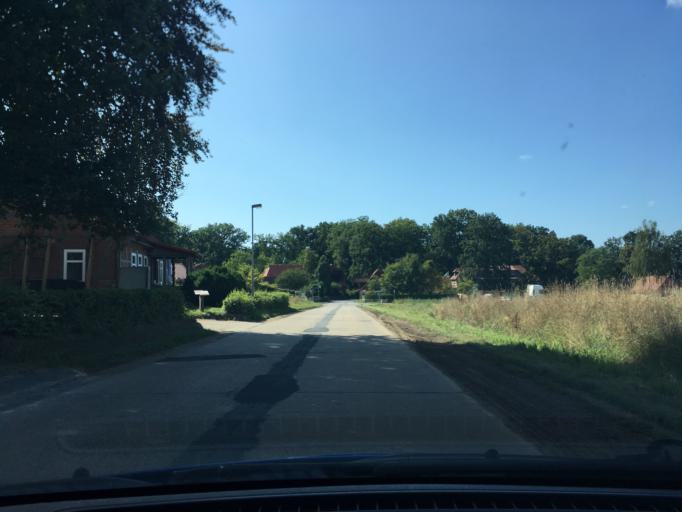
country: DE
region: Lower Saxony
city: Bergen
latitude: 52.8337
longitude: 9.9389
